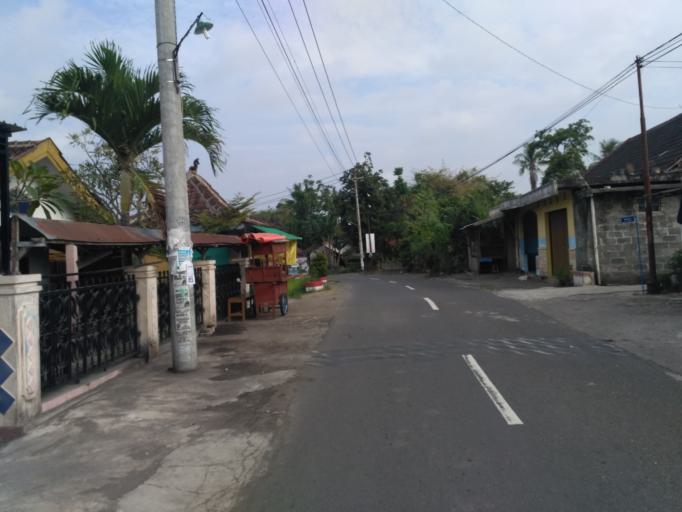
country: ID
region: Daerah Istimewa Yogyakarta
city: Melati
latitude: -7.7093
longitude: 110.3926
